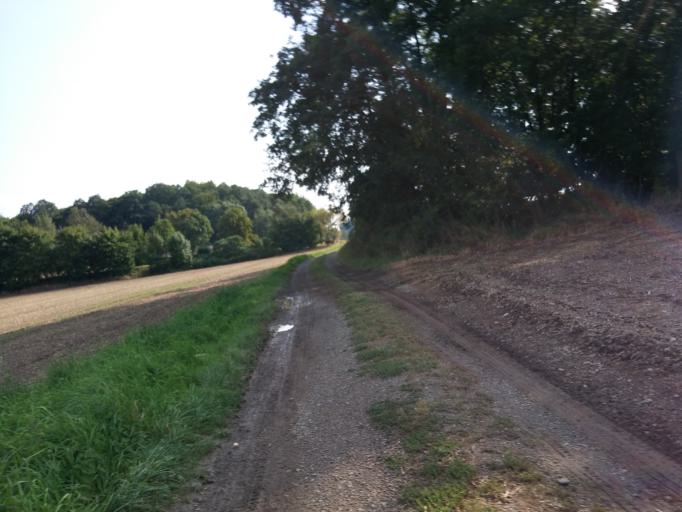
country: DE
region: Saxony
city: Elsterberg
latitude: 50.5781
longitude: 12.1344
